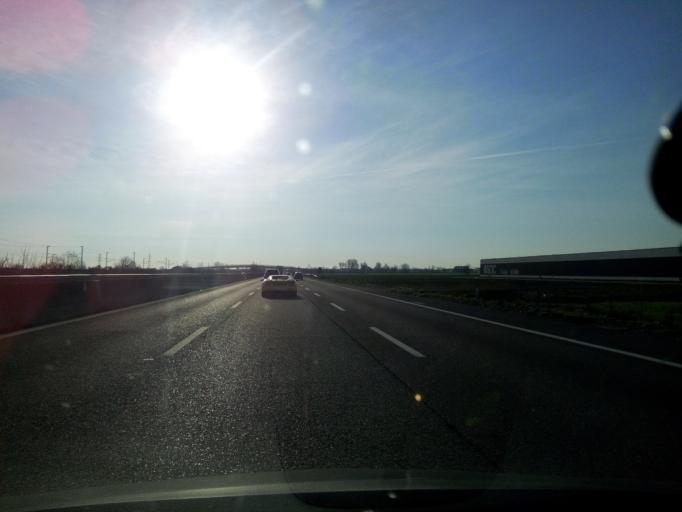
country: IT
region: Emilia-Romagna
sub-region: Provincia di Parma
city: Baganzola
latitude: 44.8582
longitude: 10.2625
